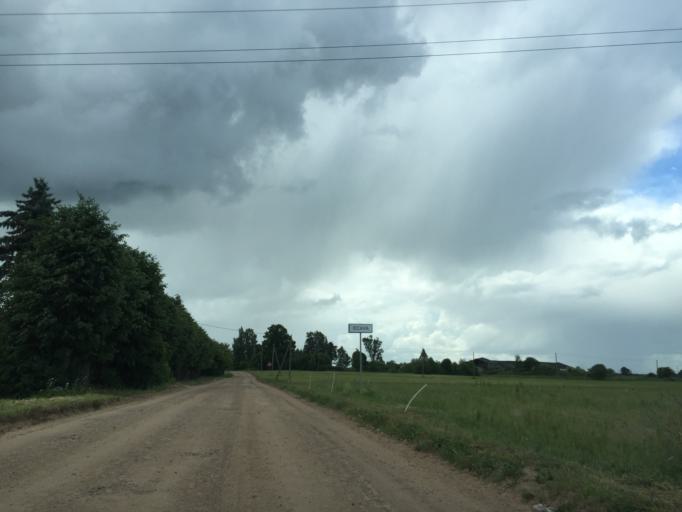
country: LV
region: Lecava
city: Iecava
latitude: 56.6098
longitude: 24.1798
